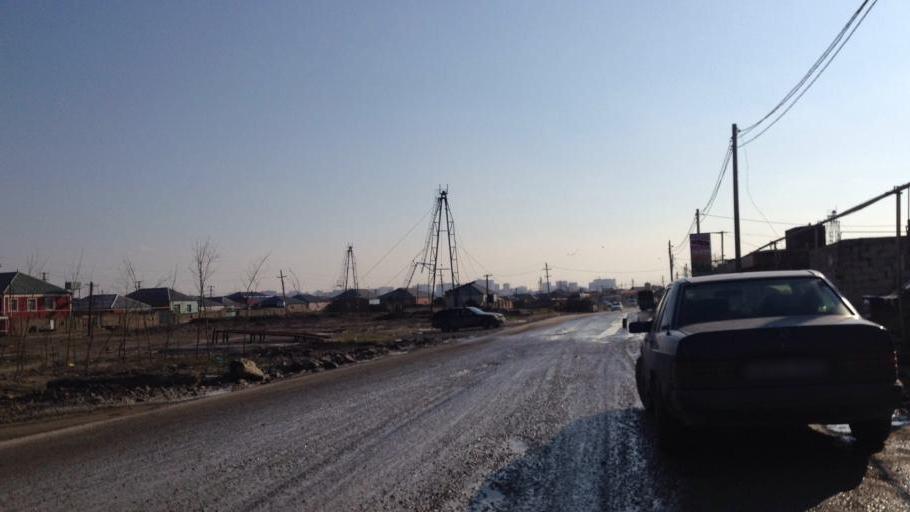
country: AZ
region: Baki
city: Balakhani
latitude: 40.4506
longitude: 49.9315
